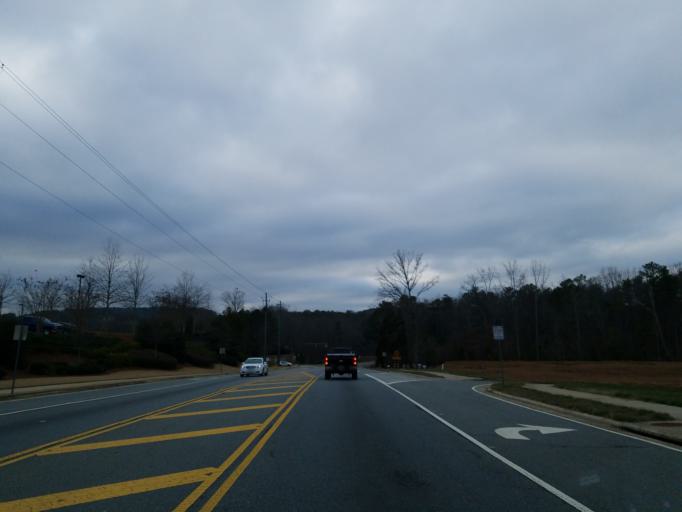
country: US
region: Georgia
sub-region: Cherokee County
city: Canton
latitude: 34.2723
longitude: -84.5020
